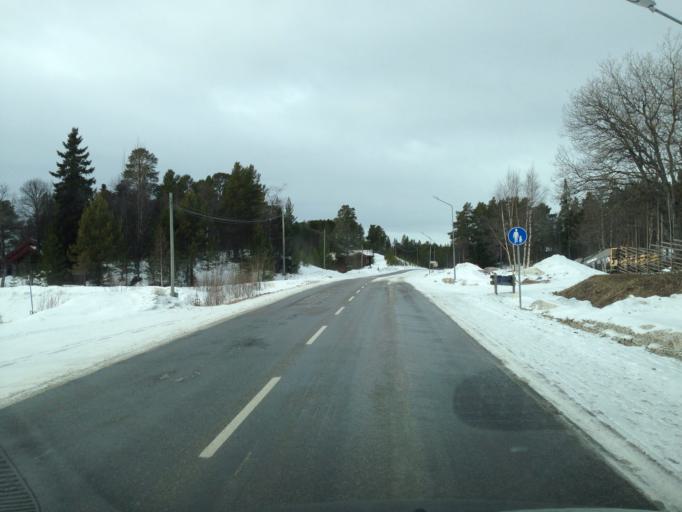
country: SE
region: Jaemtland
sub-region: Harjedalens Kommun
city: Sveg
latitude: 62.1125
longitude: 13.2679
